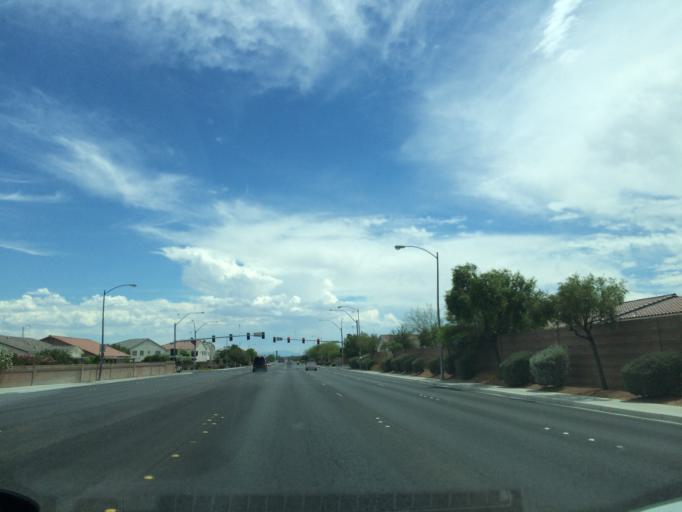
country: US
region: Nevada
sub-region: Clark County
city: North Las Vegas
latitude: 36.2555
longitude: -115.1801
